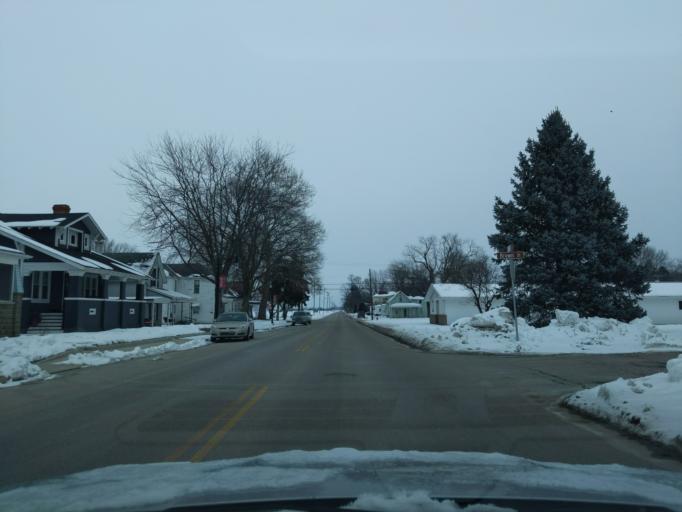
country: US
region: Indiana
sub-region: Benton County
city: Otterbein
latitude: 40.4904
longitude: -87.0952
